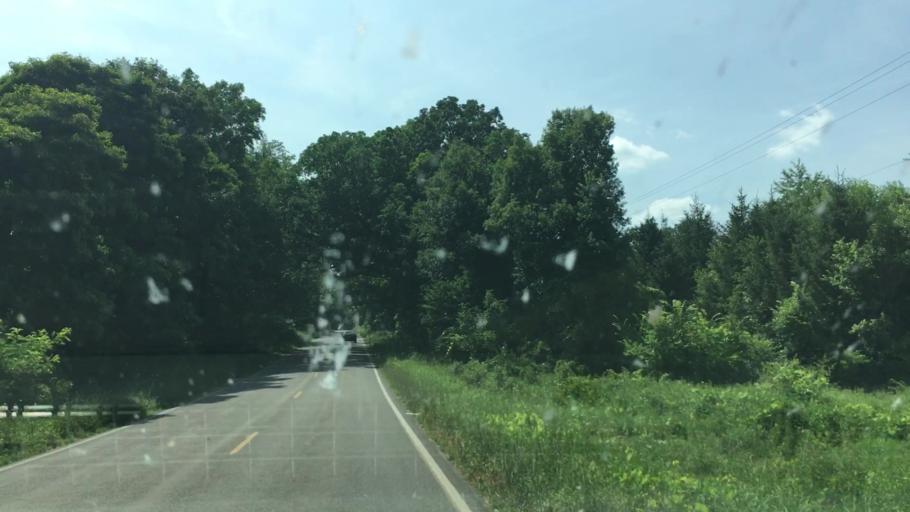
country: US
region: Michigan
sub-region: Kalamazoo County
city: Comstock Northwest
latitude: 42.4287
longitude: -85.5159
